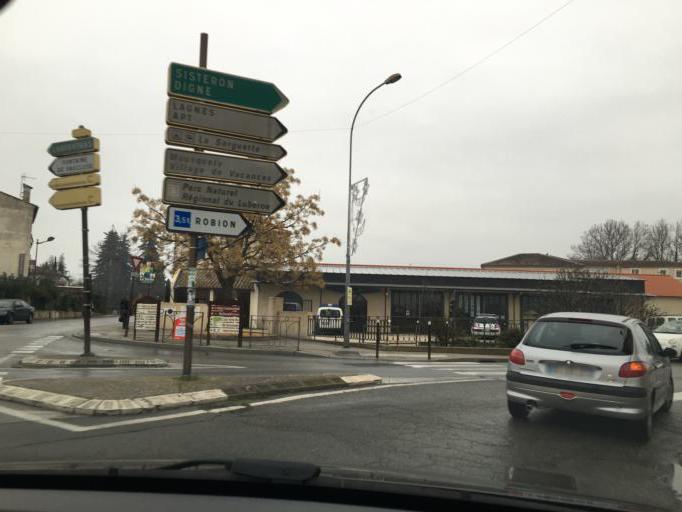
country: FR
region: Provence-Alpes-Cote d'Azur
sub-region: Departement du Vaucluse
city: L'Isle-sur-la-Sorgue
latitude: 43.9193
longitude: 5.0558
